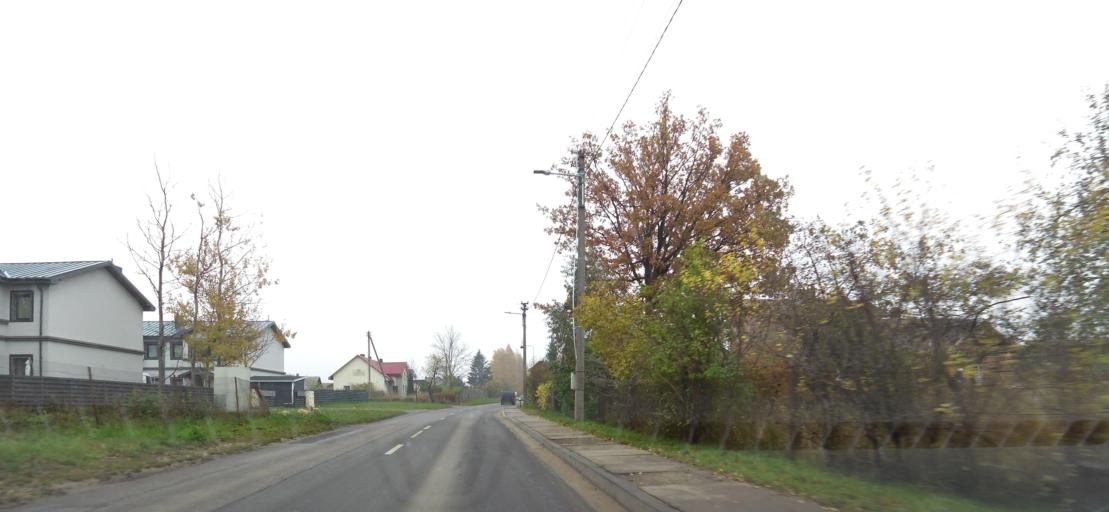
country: LT
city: Skaidiskes
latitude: 54.6598
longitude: 25.3606
